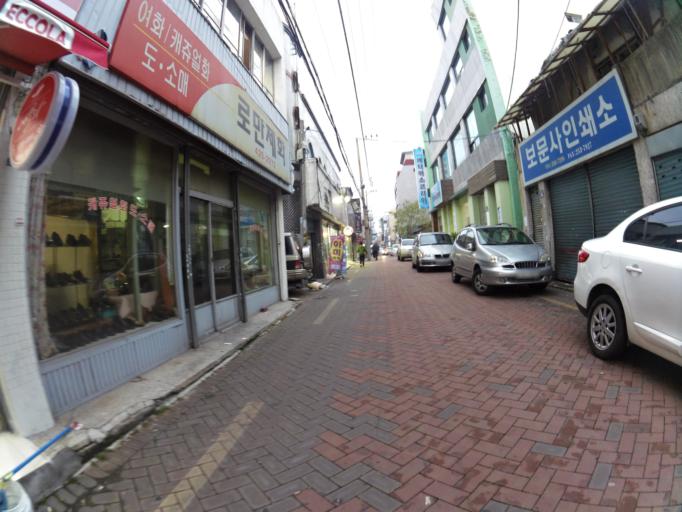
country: KR
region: Daegu
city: Daegu
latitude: 35.8729
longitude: 128.5920
